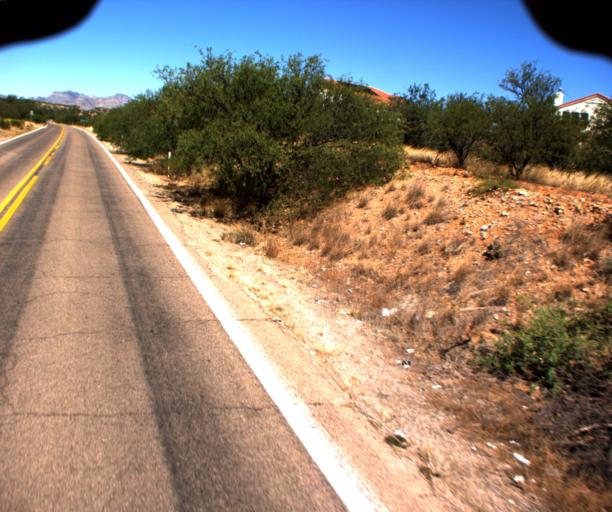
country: US
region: Arizona
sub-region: Santa Cruz County
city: Rio Rico
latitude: 31.4302
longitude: -110.9717
